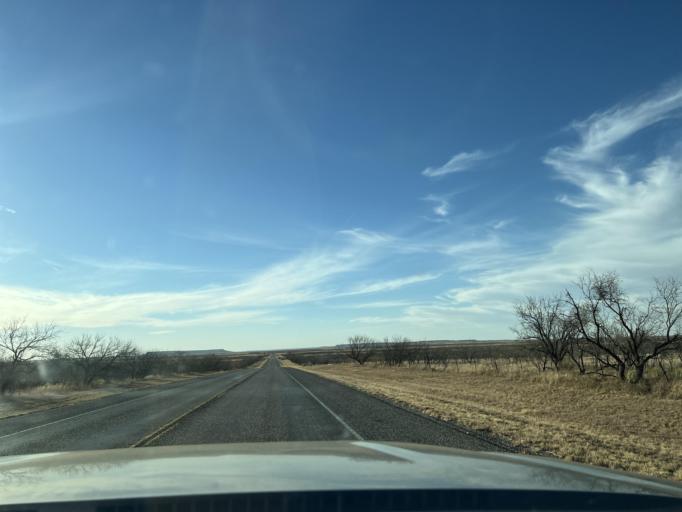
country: US
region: Texas
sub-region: Borden County
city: Gail
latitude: 32.7692
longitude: -101.3189
